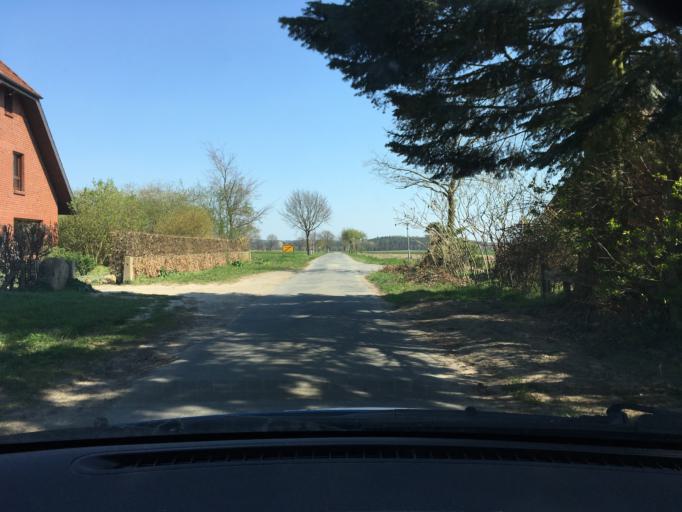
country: DE
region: Lower Saxony
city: Reinstorf
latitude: 53.2014
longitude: 10.5848
